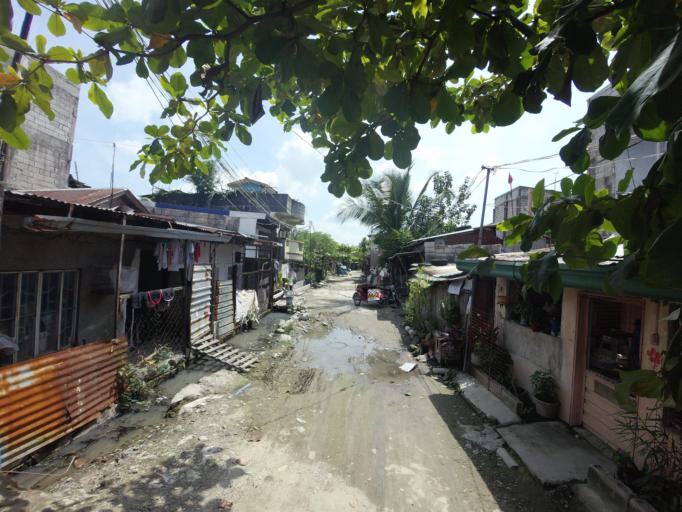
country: PH
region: Calabarzon
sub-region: Province of Rizal
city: Taytay
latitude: 14.5346
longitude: 121.1111
